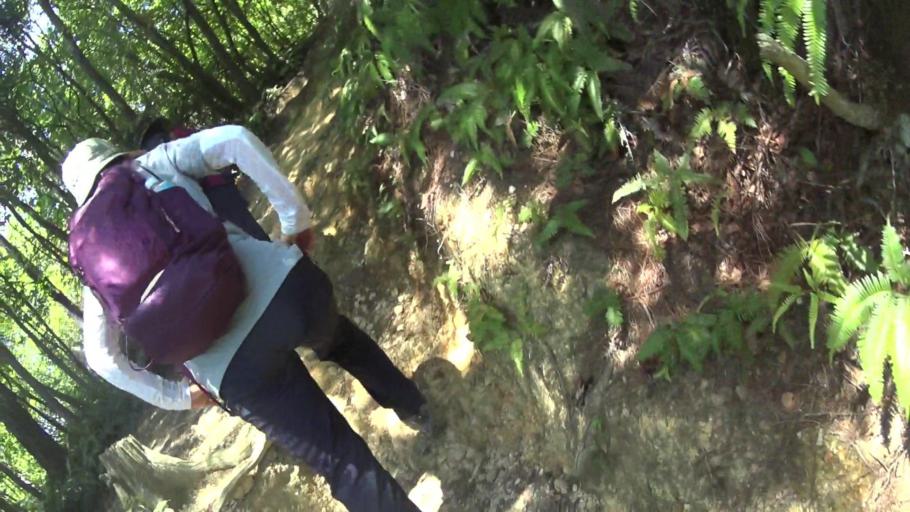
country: JP
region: Kyoto
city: Kyoto
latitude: 35.0084
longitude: 135.8020
